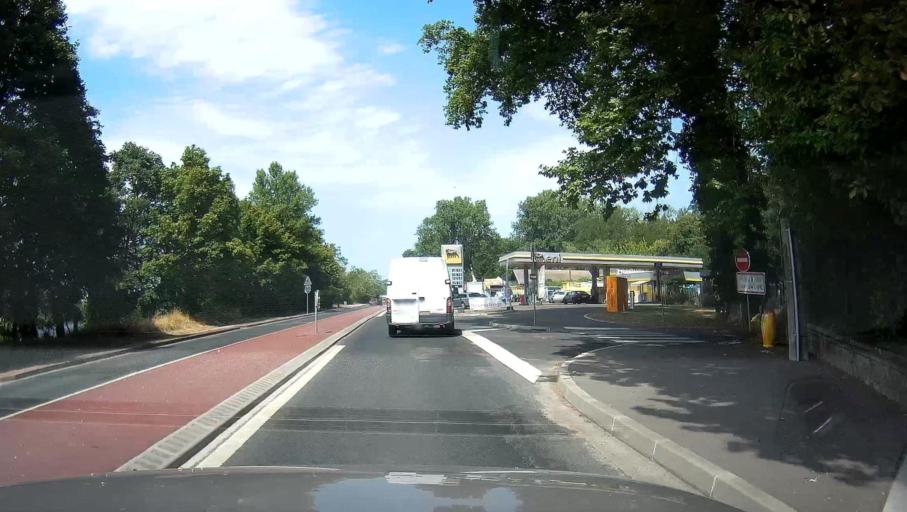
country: FR
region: Rhone-Alpes
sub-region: Departement du Rhone
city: Fleurieu-sur-Saone
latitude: 45.8548
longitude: 4.8393
